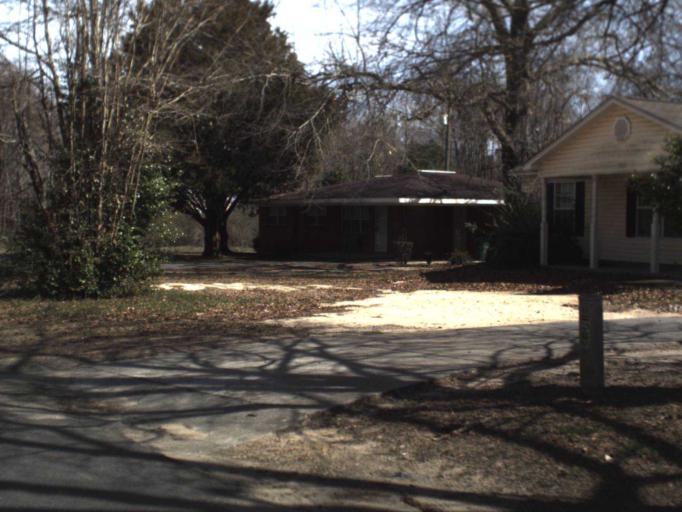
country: US
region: Florida
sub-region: Jackson County
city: Graceville
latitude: 30.9681
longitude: -85.5112
